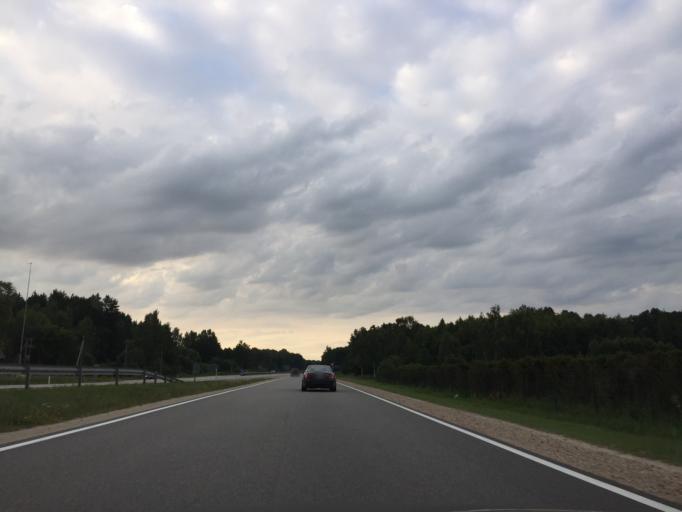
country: LV
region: Babite
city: Pinki
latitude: 56.9267
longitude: 23.9157
